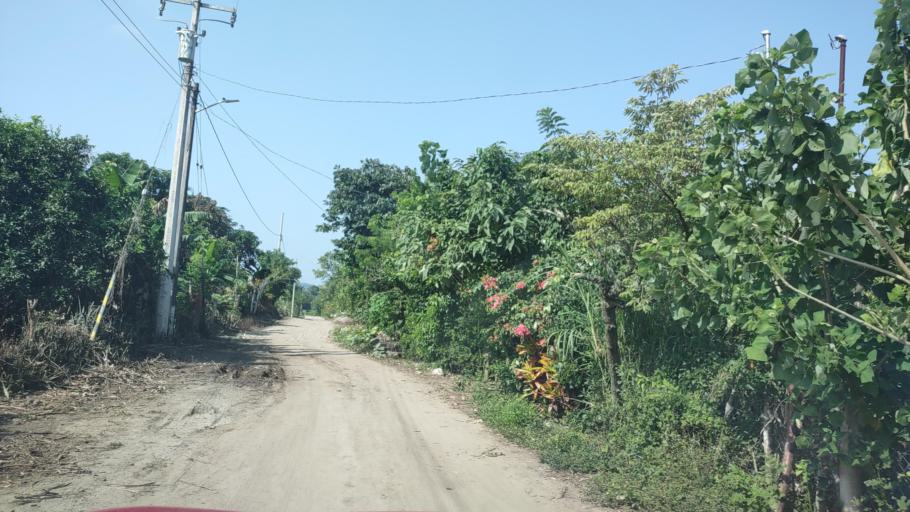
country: MX
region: Puebla
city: Espinal
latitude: 20.2402
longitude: -97.3468
